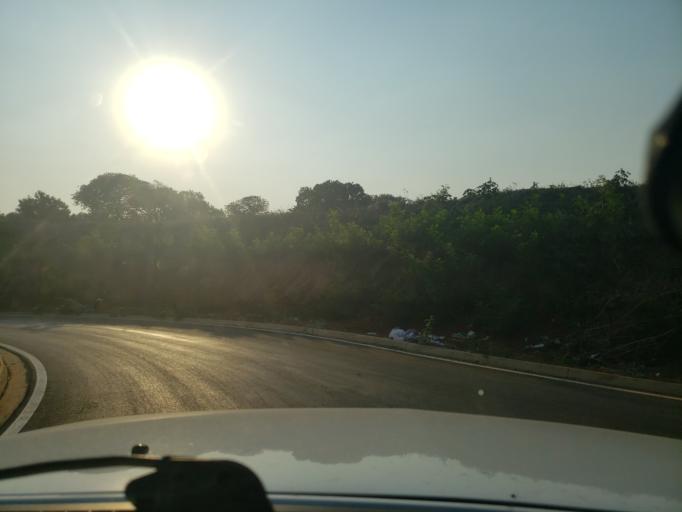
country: BR
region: Sao Paulo
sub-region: Moji-Guacu
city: Mogi-Gaucu
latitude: -22.3253
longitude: -46.9499
